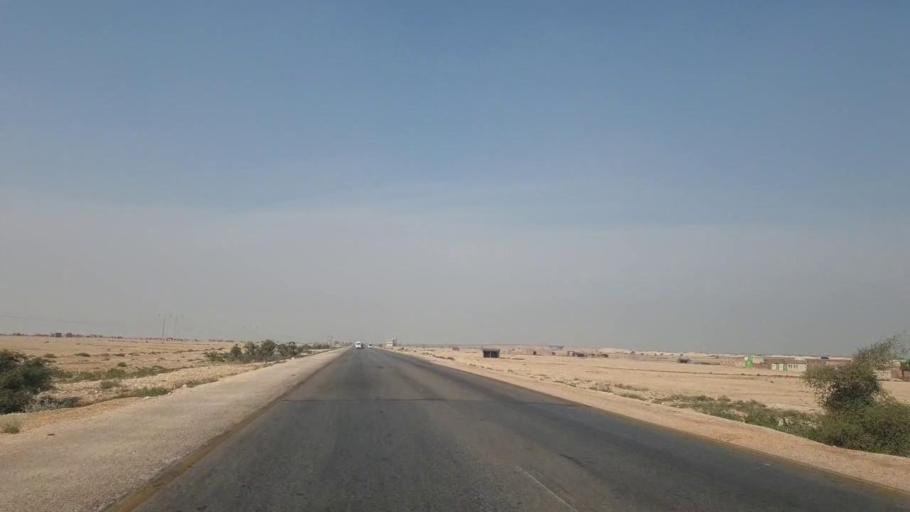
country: PK
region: Sindh
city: Hala
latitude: 25.8463
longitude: 68.2621
